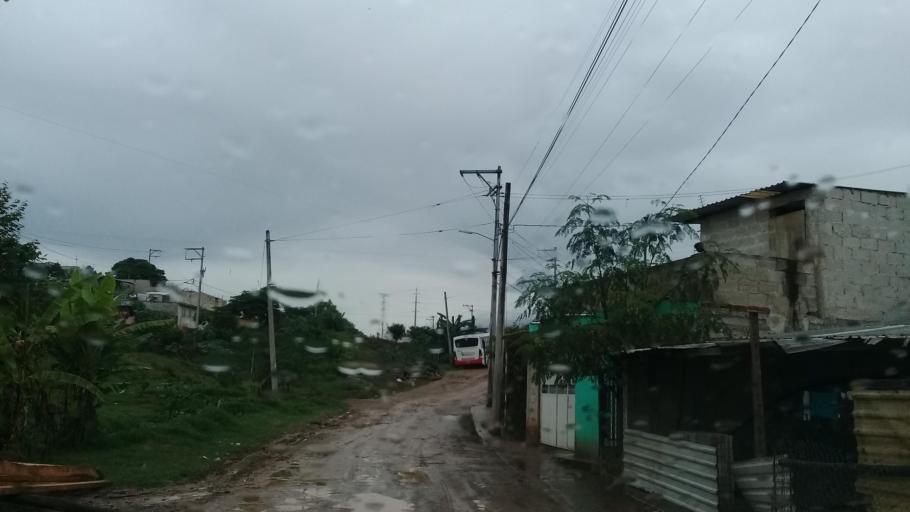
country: MX
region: Veracruz
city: El Castillo
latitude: 19.5672
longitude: -96.8871
